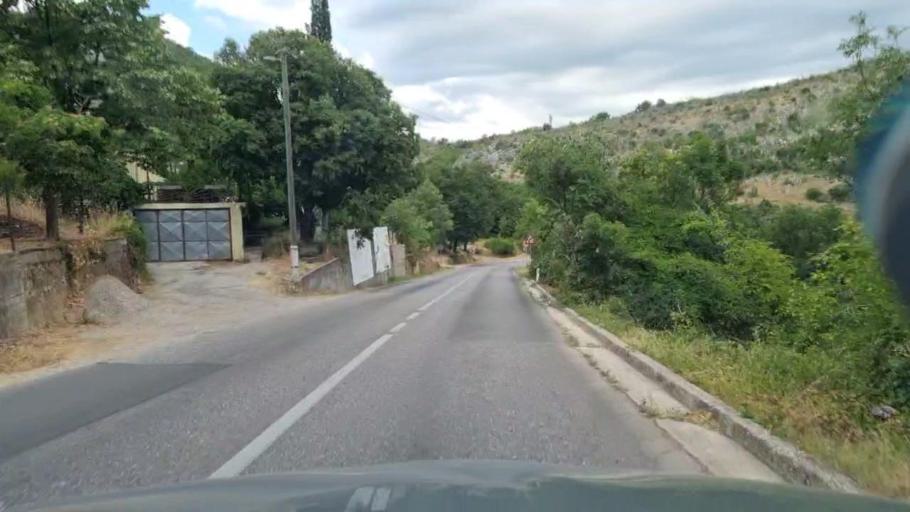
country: BA
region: Federation of Bosnia and Herzegovina
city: Rodoc
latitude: 43.3245
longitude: 17.7917
